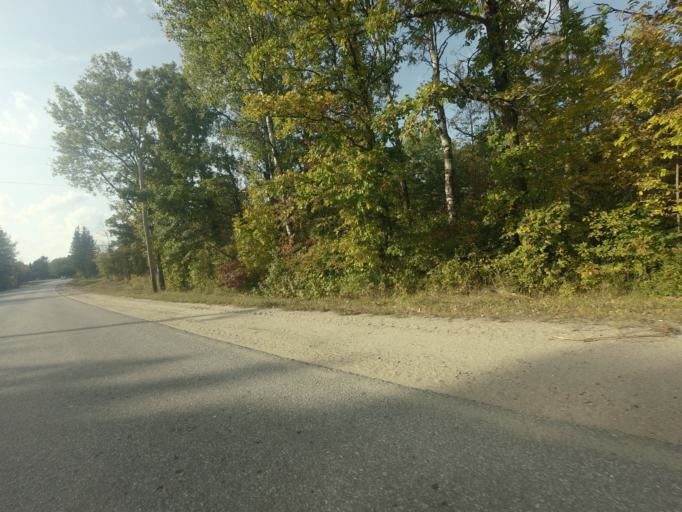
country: CA
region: Quebec
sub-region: Outaouais
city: Maniwaki
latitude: 46.3651
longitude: -75.9937
